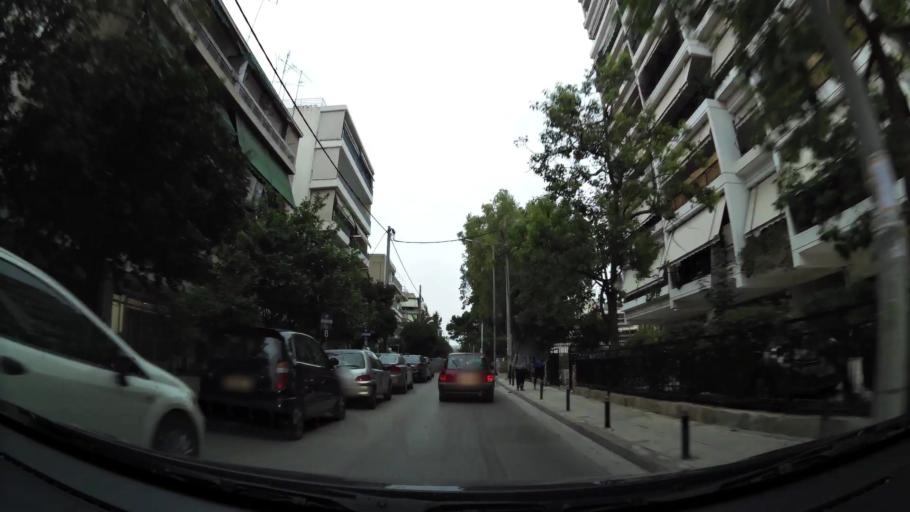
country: GR
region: Attica
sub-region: Nomos Piraios
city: Agios Ioannis Rentis
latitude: 37.9610
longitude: 23.6711
